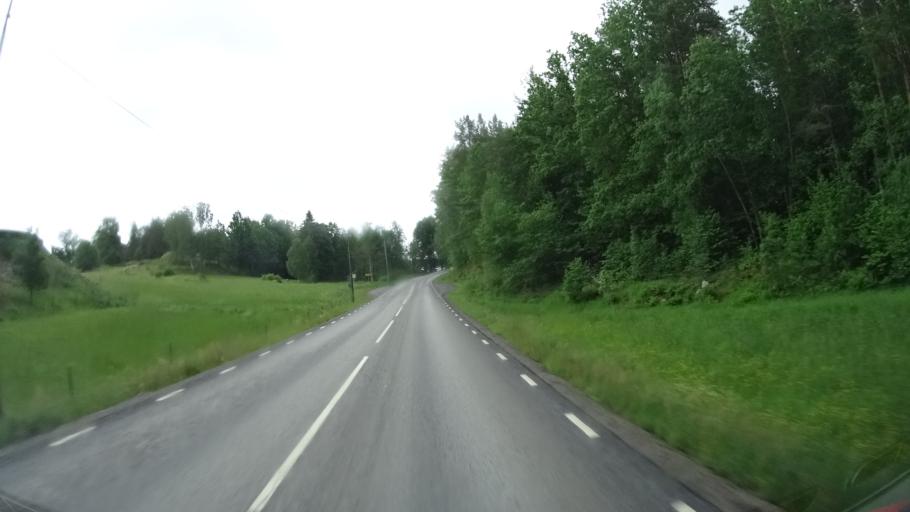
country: SE
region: Kalmar
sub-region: Oskarshamns Kommun
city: Oskarshamn
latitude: 57.3909
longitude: 16.2189
